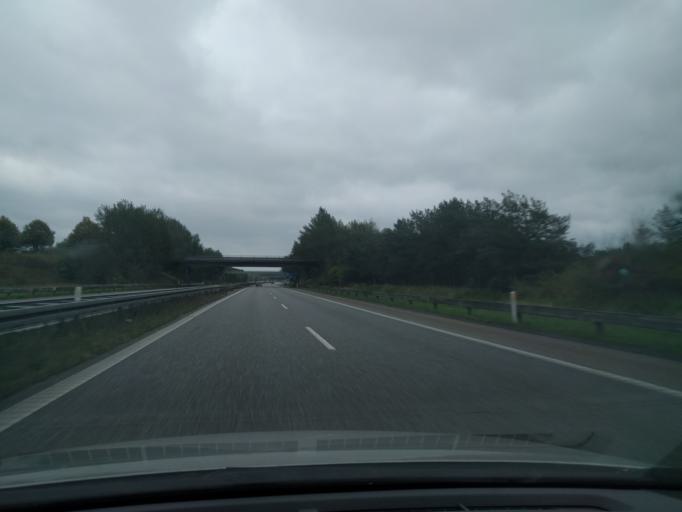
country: DK
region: Zealand
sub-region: Soro Kommune
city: Soro
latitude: 55.4566
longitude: 11.5500
